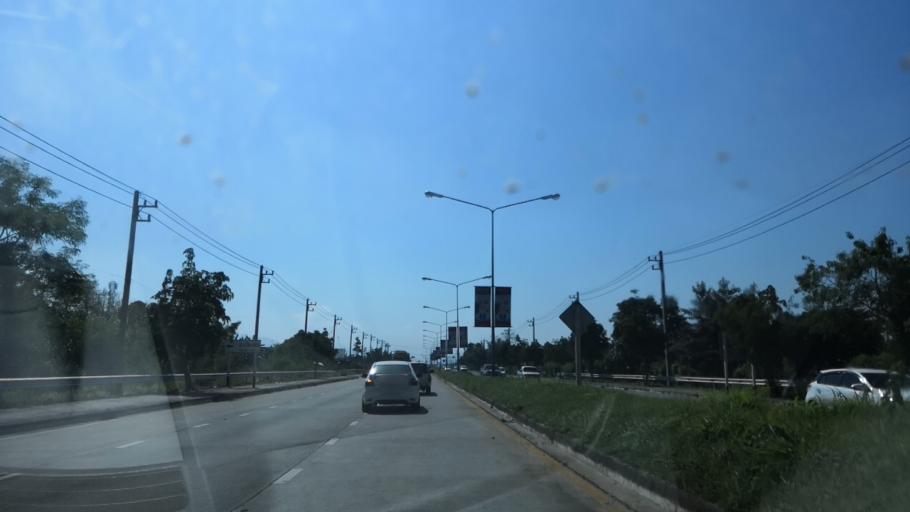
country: TH
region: Chiang Rai
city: Chiang Rai
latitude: 19.8989
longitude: 99.8573
